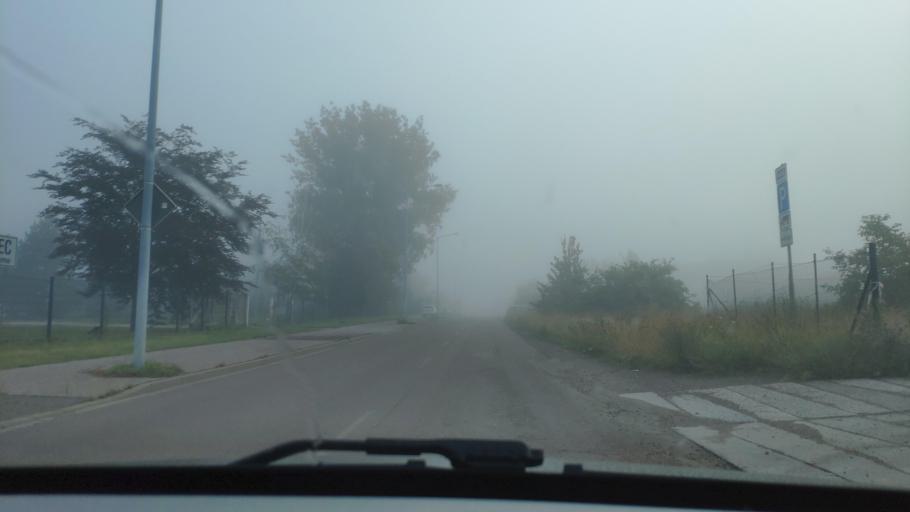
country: DE
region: Saxony-Anhalt
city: Bernburg
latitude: 51.7747
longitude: 11.7330
